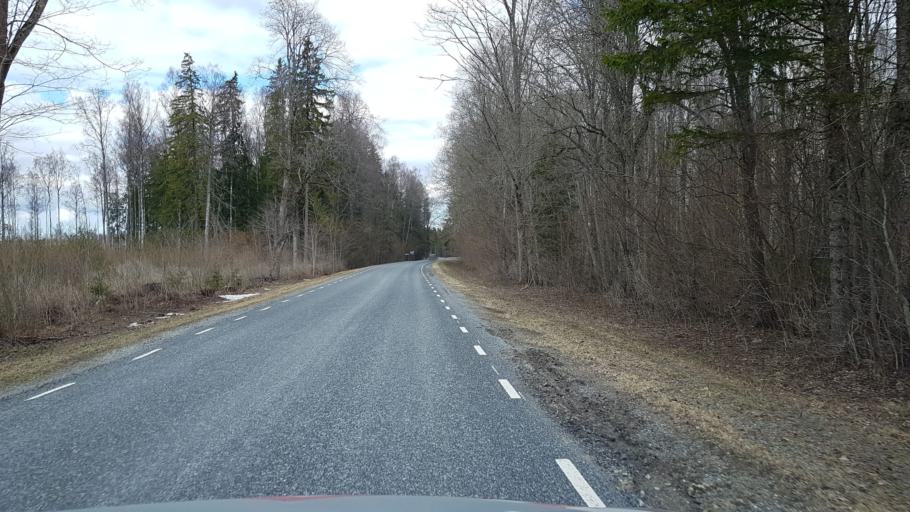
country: EE
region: Laeaene-Virumaa
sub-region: Tamsalu vald
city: Tamsalu
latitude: 59.1915
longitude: 26.1303
